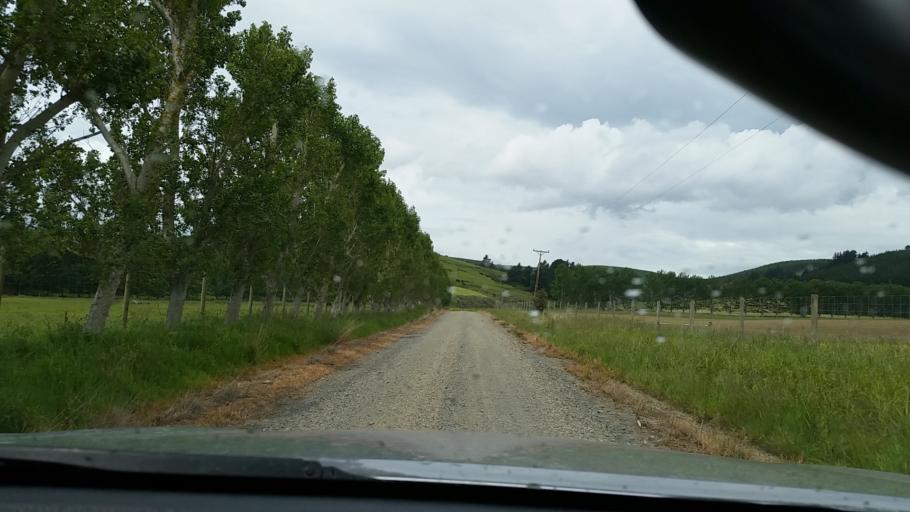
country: NZ
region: Southland
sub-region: Southland District
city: Winton
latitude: -45.9115
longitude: 168.1658
